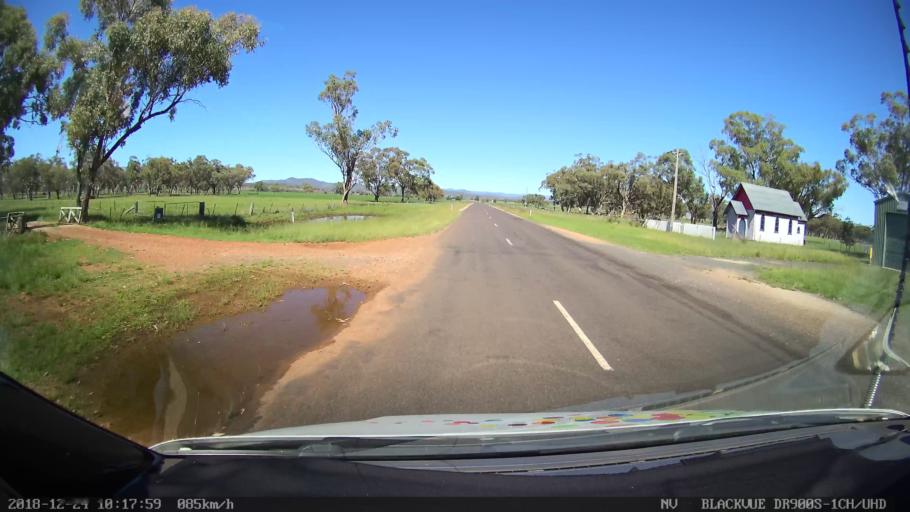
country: AU
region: New South Wales
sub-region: Liverpool Plains
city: Quirindi
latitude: -31.7220
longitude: 150.5832
